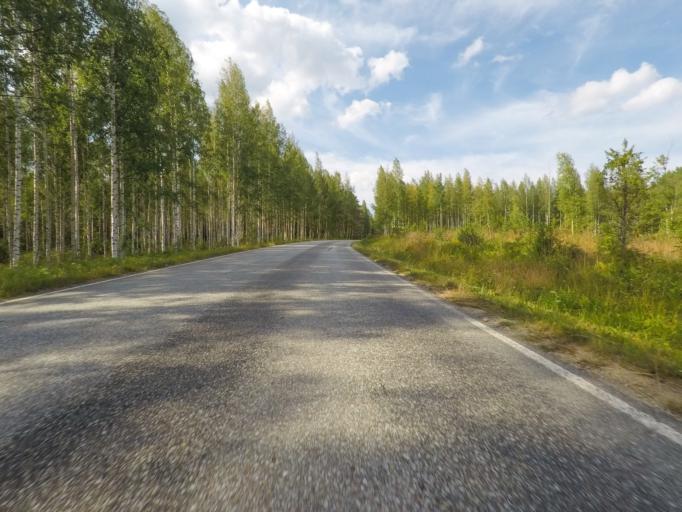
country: FI
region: Southern Savonia
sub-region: Mikkeli
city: Puumala
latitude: 61.7042
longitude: 28.2115
